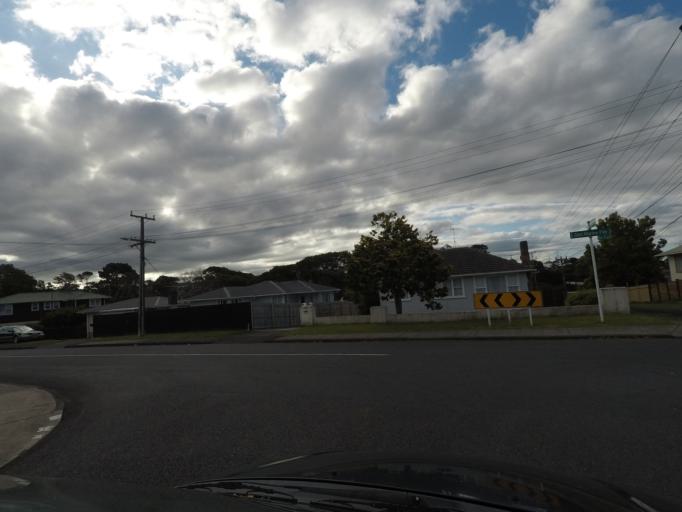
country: NZ
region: Auckland
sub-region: Auckland
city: Rosebank
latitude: -36.8824
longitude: 174.6567
